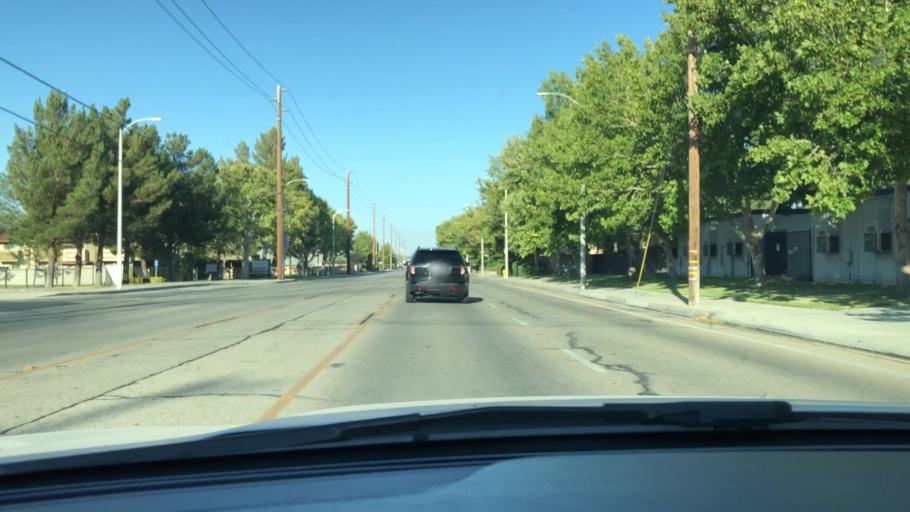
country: US
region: California
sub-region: Los Angeles County
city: Lancaster
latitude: 34.6821
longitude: -118.1732
